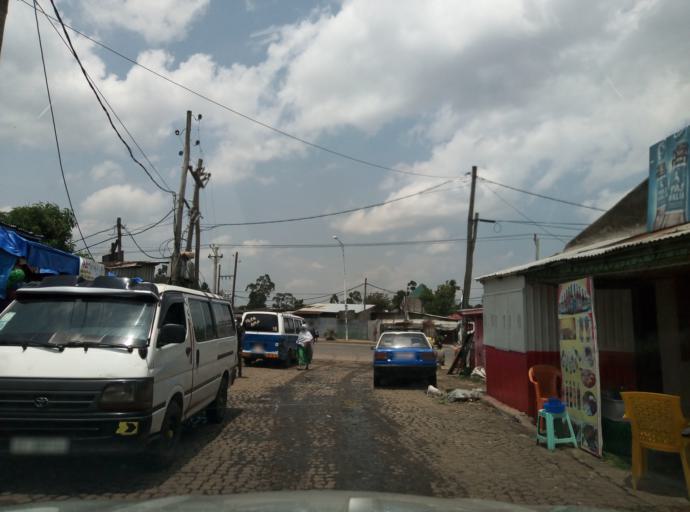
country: ET
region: Adis Abeba
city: Addis Ababa
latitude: 8.9451
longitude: 38.7561
